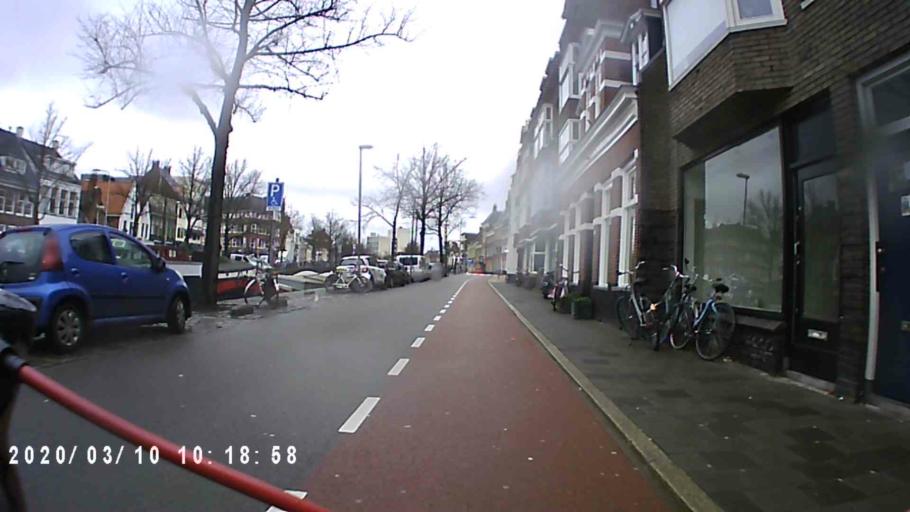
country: NL
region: Groningen
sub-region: Gemeente Groningen
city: Groningen
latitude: 53.2193
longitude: 6.5720
